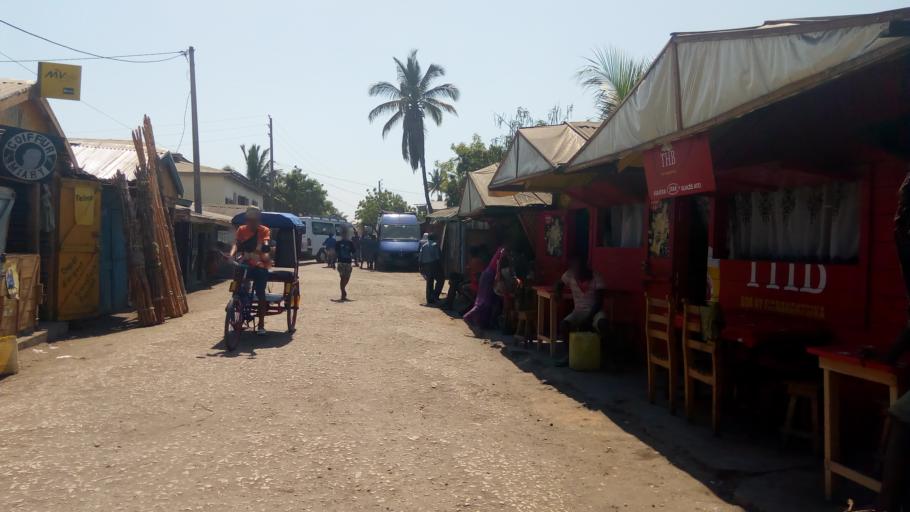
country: MG
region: Menabe
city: Morondava
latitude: -20.2912
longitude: 44.2767
